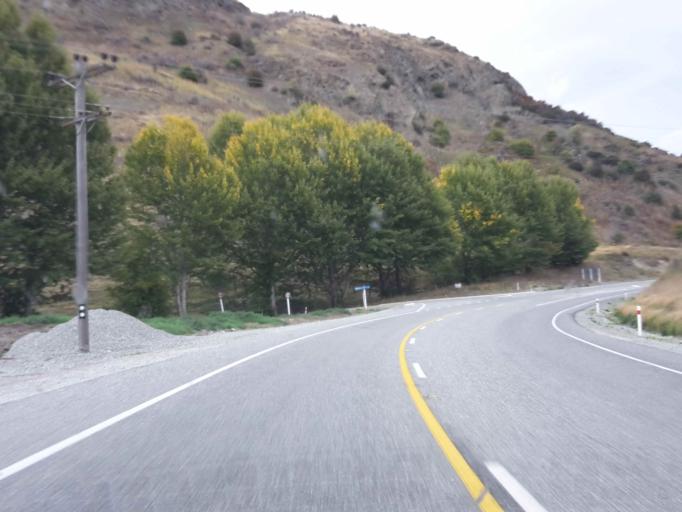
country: NZ
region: Otago
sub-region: Queenstown-Lakes District
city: Arrowtown
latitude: -44.9820
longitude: 168.8377
